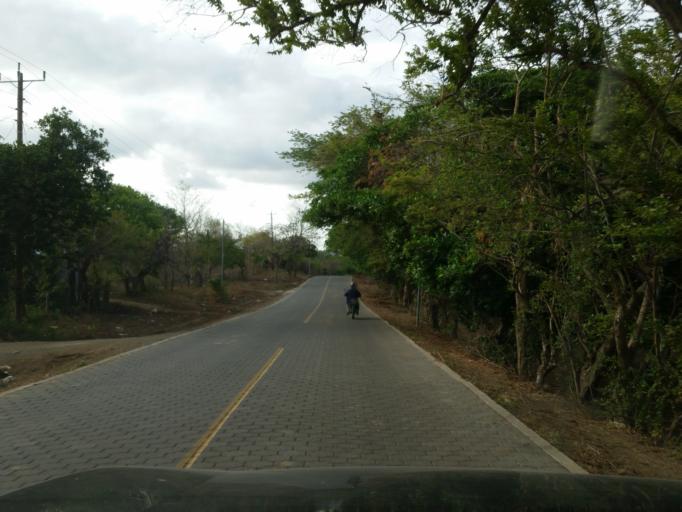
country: NI
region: Rivas
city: Tola
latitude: 11.4322
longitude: -85.9428
